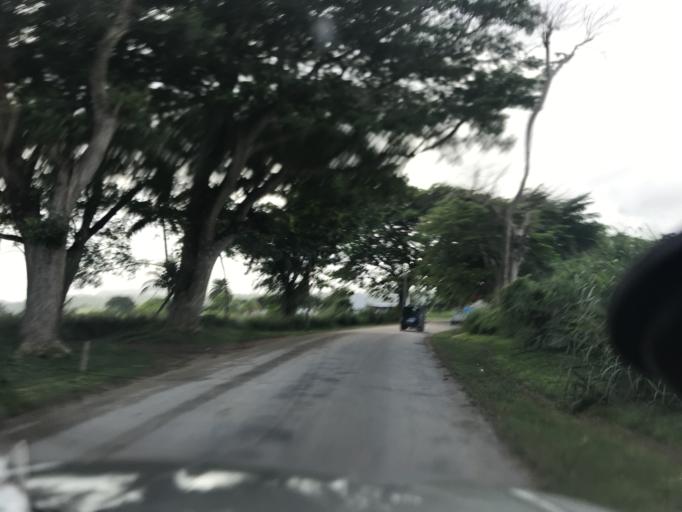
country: VU
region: Shefa
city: Port-Vila
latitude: -17.7058
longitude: 168.3149
